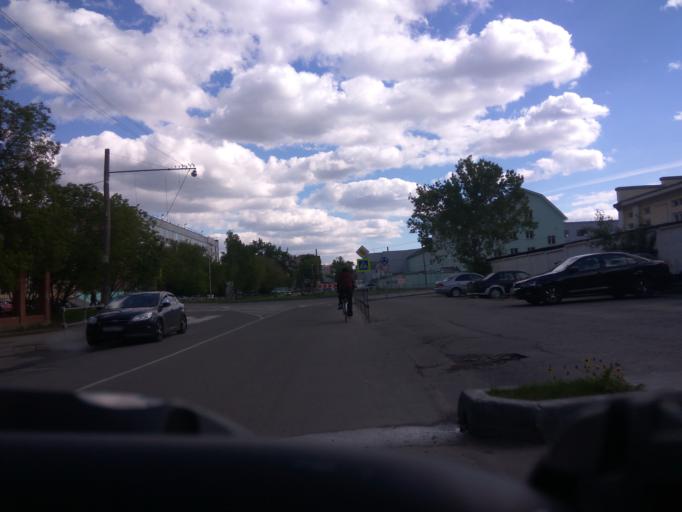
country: RU
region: Moscow
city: Mar'ina Roshcha
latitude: 55.8034
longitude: 37.5957
